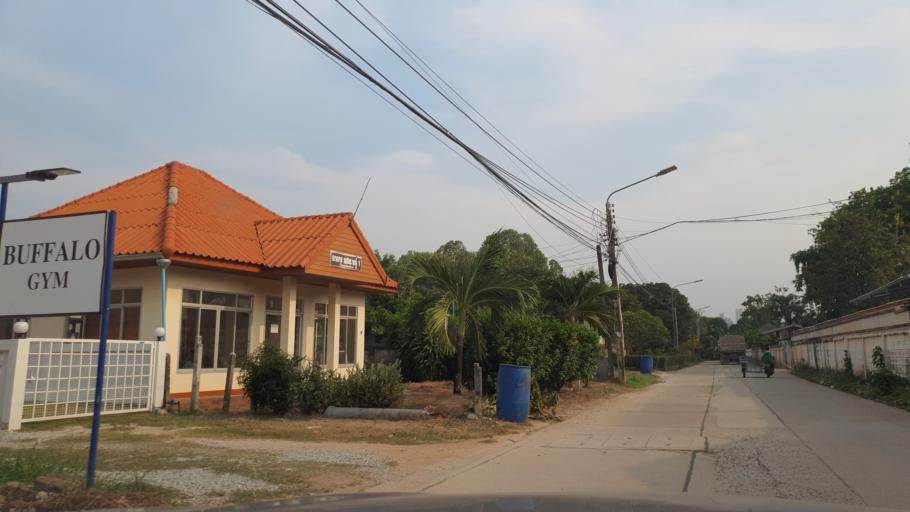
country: TH
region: Rayong
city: Rayong
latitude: 12.6189
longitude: 101.4031
